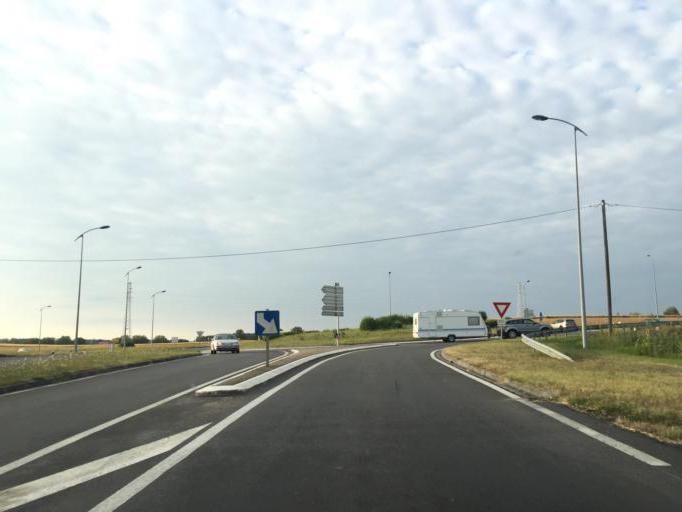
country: FR
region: Auvergne
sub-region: Departement de l'Allier
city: Varennes-sur-Allier
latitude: 46.3039
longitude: 3.4251
